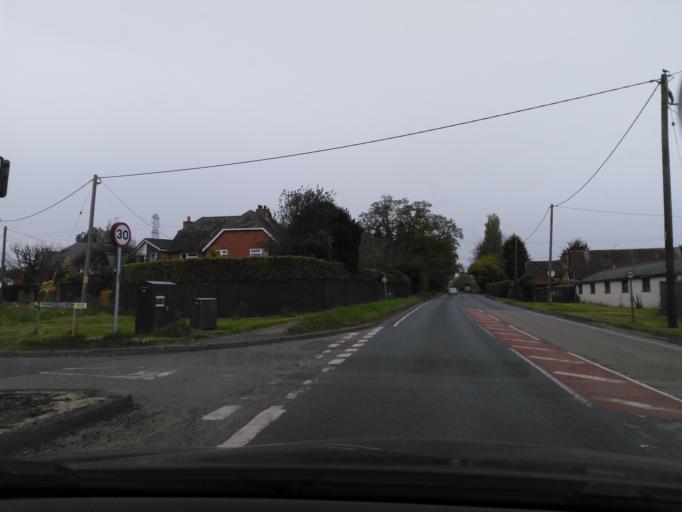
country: GB
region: England
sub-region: Hampshire
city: Tadley
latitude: 51.3217
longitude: -1.1234
